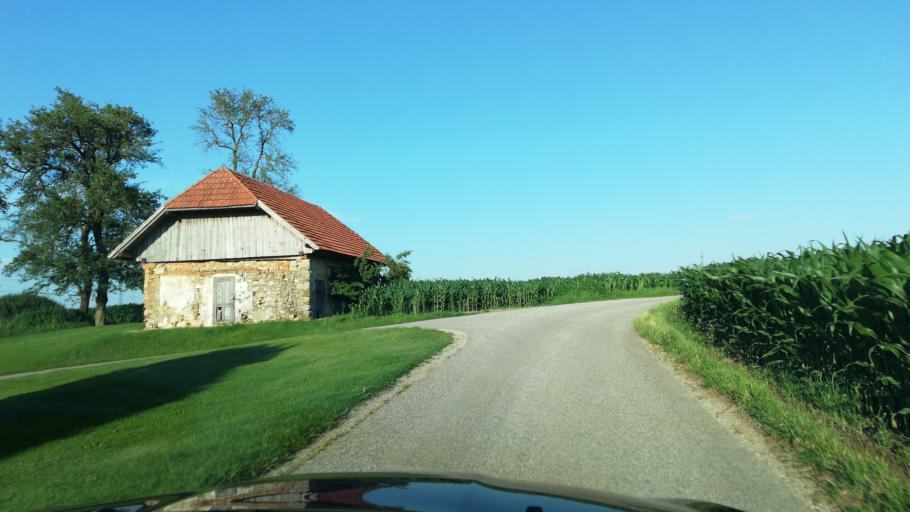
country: AT
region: Upper Austria
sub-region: Wels-Land
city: Sattledt
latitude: 48.0805
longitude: 14.0305
